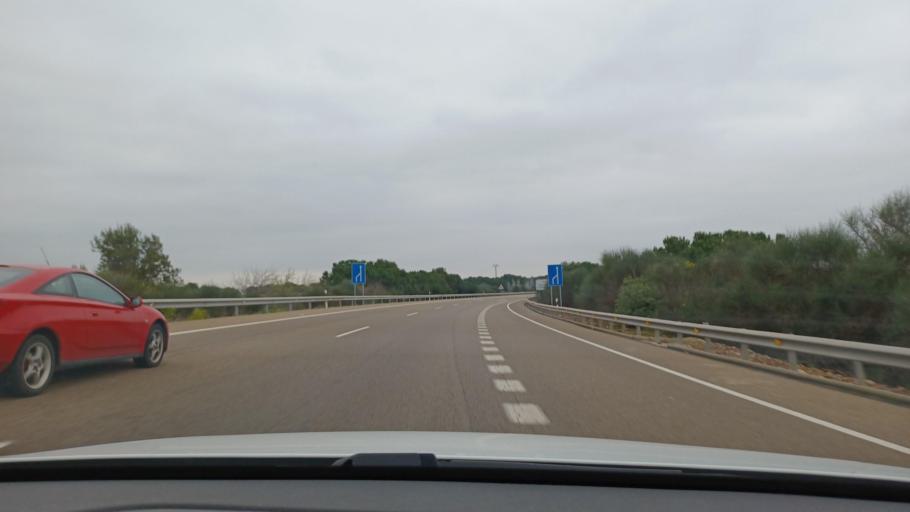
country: ES
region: Valencia
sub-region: Provincia de Castello
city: Nules
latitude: 39.8625
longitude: -0.1666
